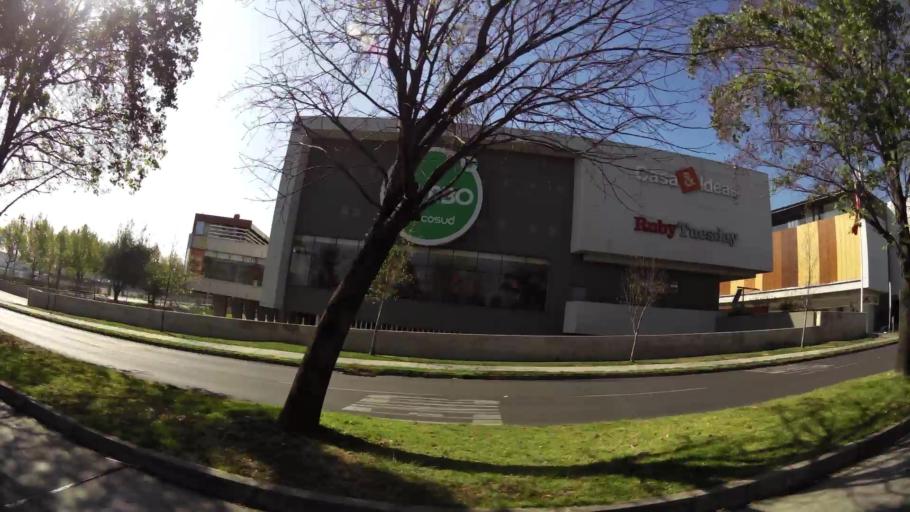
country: CL
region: Santiago Metropolitan
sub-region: Provincia de Santiago
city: Villa Presidente Frei, Nunoa, Santiago, Chile
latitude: -33.4028
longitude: -70.5144
